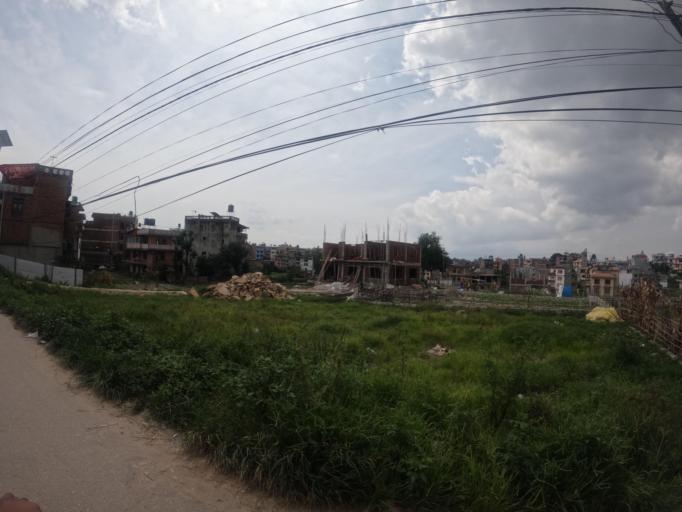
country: NP
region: Central Region
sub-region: Bagmati Zone
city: Bhaktapur
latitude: 27.6870
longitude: 85.3856
